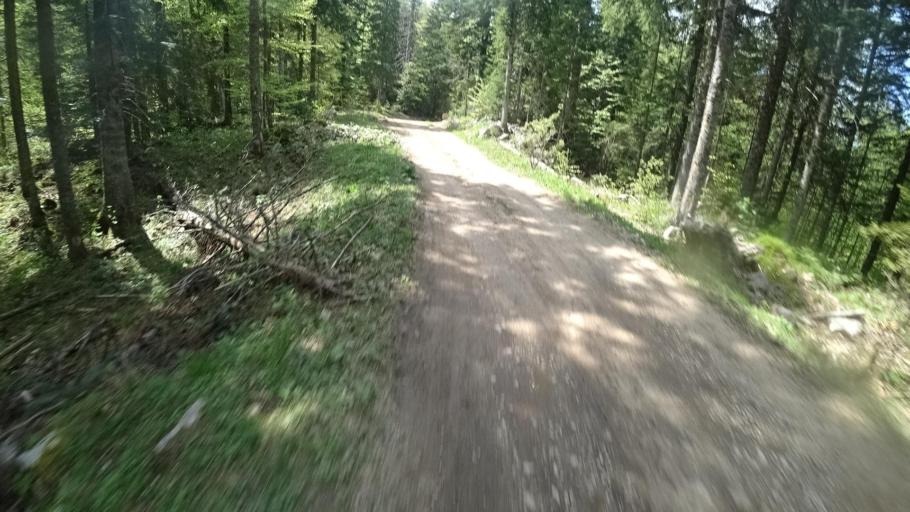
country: BA
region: Republika Srpska
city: Sipovo
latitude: 44.1478
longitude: 17.0294
